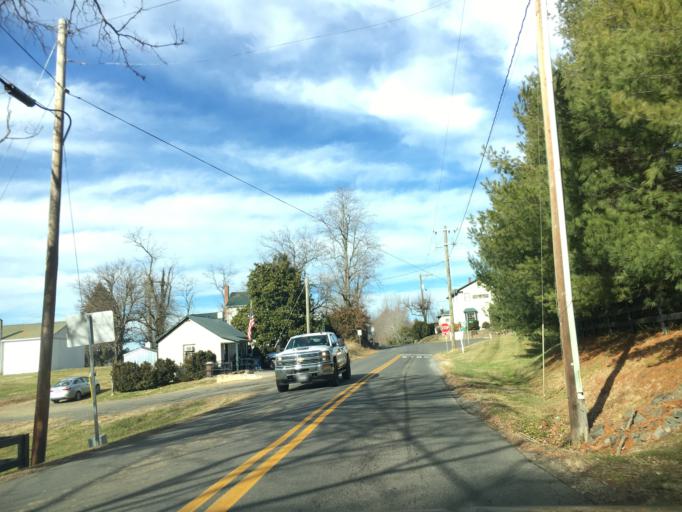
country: US
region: Virginia
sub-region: Fauquier County
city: Marshall
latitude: 38.7520
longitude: -77.9637
